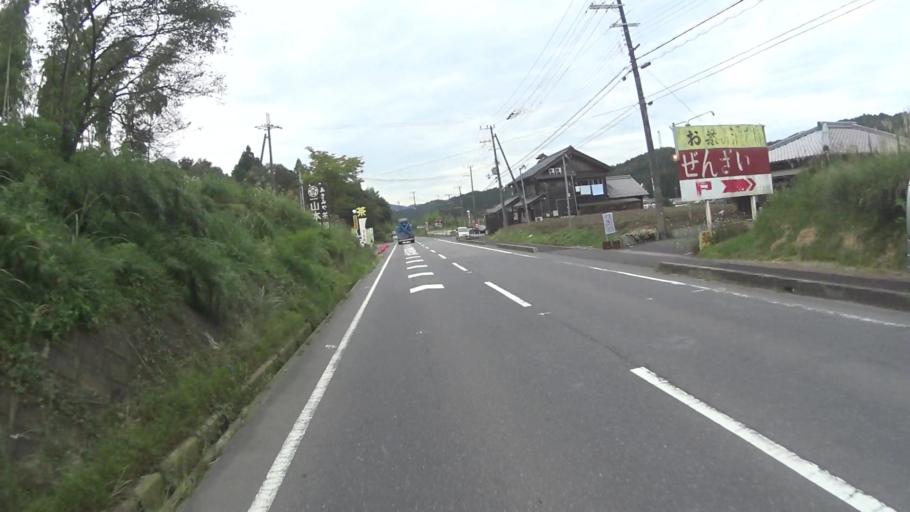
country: JP
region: Shiga Prefecture
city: Kusatsu
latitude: 34.8541
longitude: 135.9919
